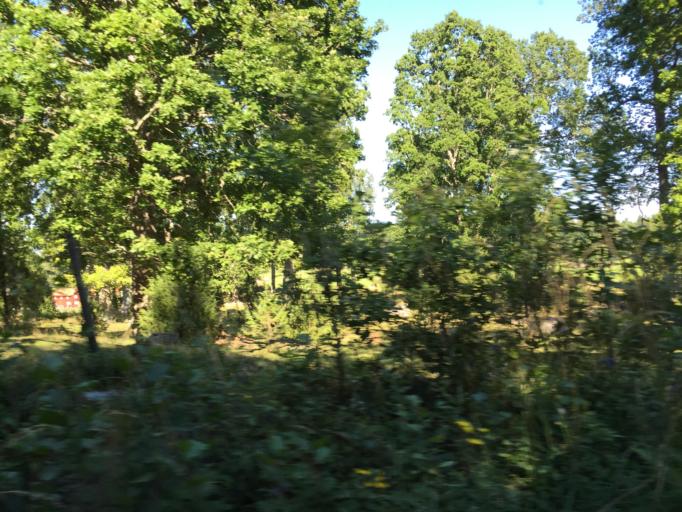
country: SE
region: OEstergoetland
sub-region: Finspangs Kommun
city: Finspang
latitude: 58.8923
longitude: 15.7088
